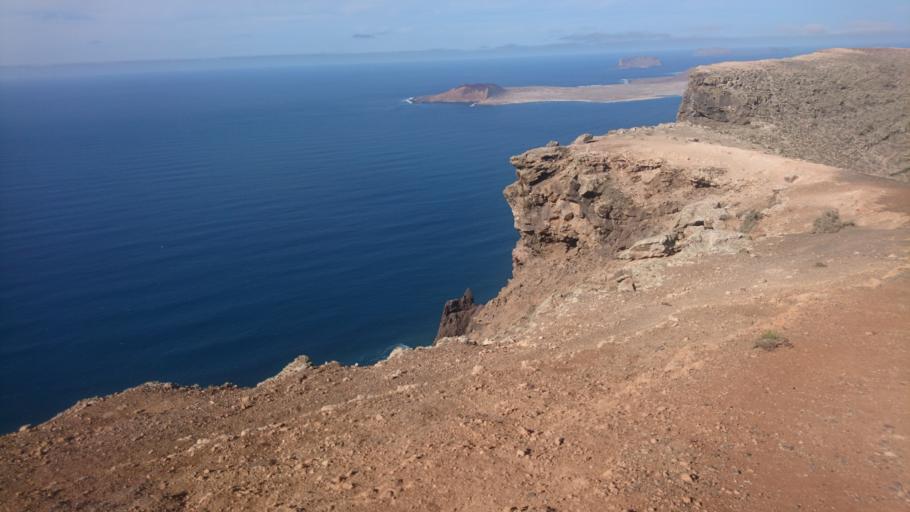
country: ES
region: Canary Islands
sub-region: Provincia de Las Palmas
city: Haria
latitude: 29.1700
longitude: -13.5121
